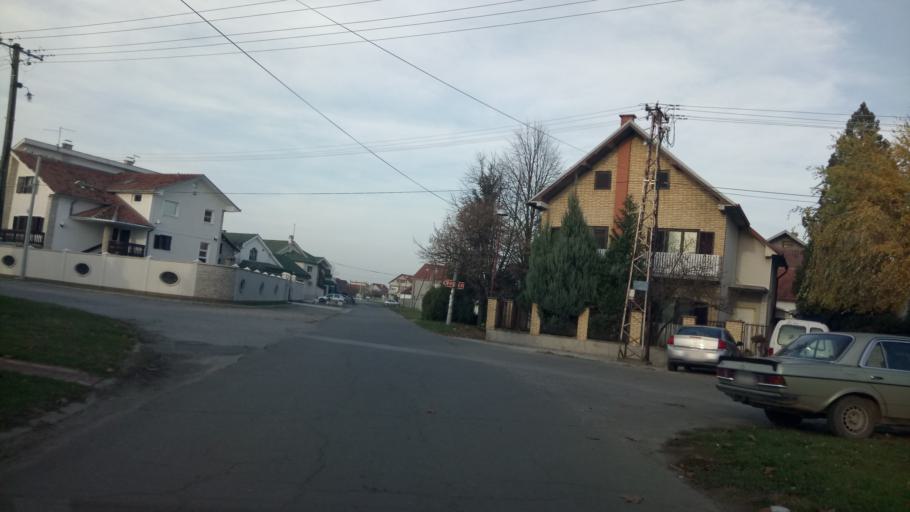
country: RS
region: Autonomna Pokrajina Vojvodina
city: Nova Pazova
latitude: 44.9343
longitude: 20.2209
